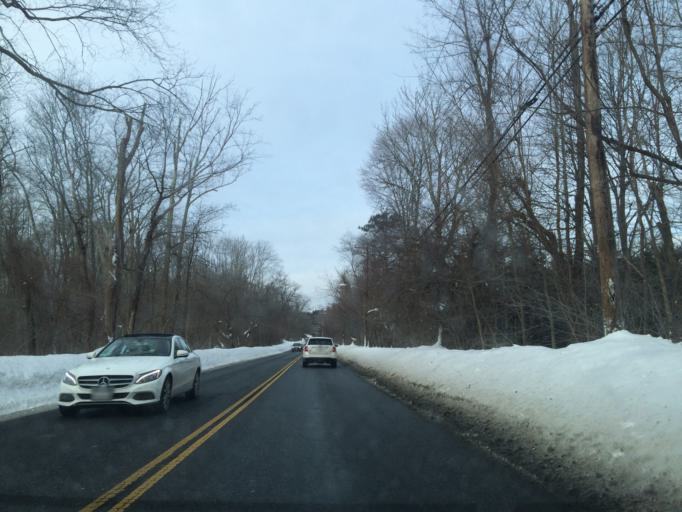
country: US
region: Massachusetts
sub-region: Middlesex County
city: Weston
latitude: 42.3409
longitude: -71.2735
